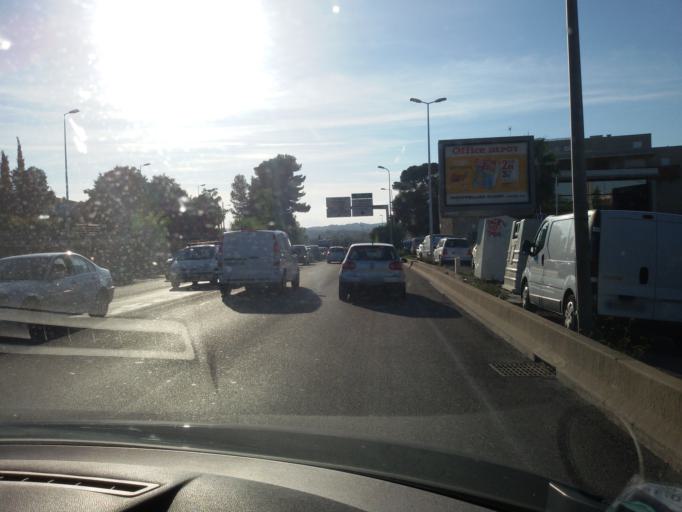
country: FR
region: Languedoc-Roussillon
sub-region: Departement de l'Herault
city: Juvignac
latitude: 43.6116
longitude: 3.8280
